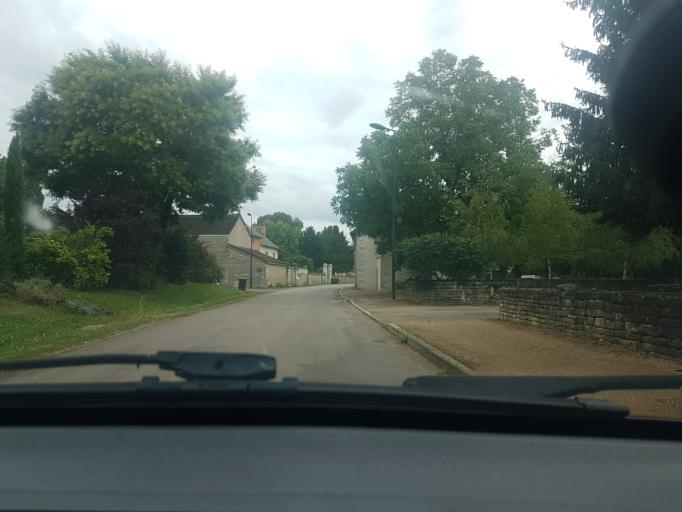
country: FR
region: Bourgogne
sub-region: Departement de Saone-et-Loire
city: Fontaines
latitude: 46.8624
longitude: 4.7607
